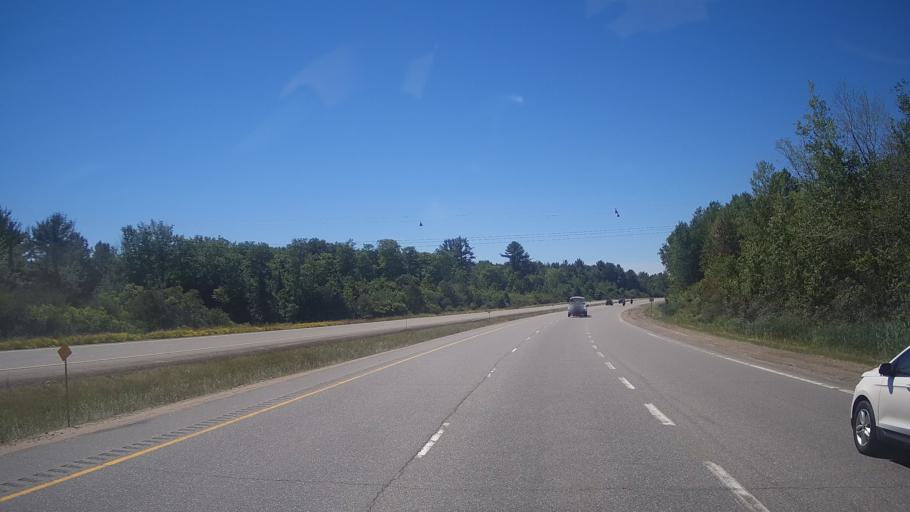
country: CA
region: Ontario
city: Bracebridge
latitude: 45.0478
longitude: -79.2870
